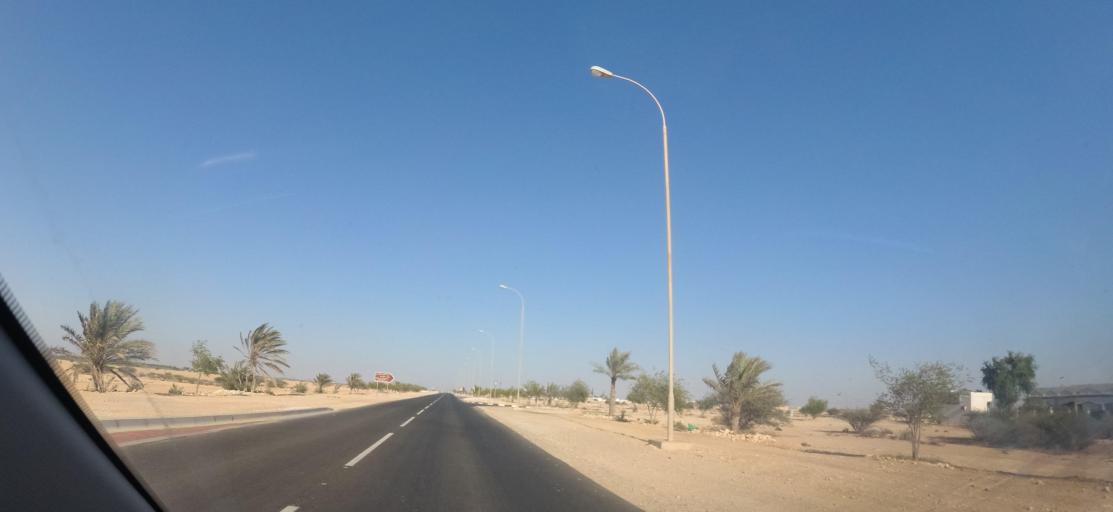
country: QA
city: Al Ghuwayriyah
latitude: 25.8325
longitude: 51.2523
